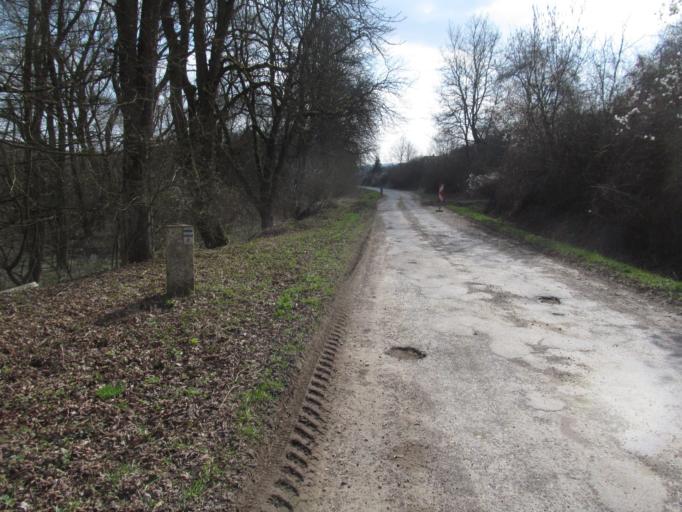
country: HU
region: Borsod-Abauj-Zemplen
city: Putnok
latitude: 48.3132
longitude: 20.4395
